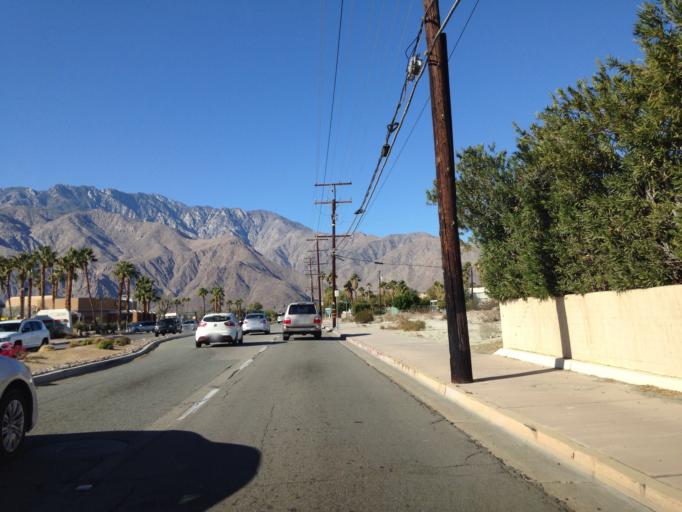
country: US
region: California
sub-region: Riverside County
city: Palm Springs
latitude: 33.8449
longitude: -116.5251
